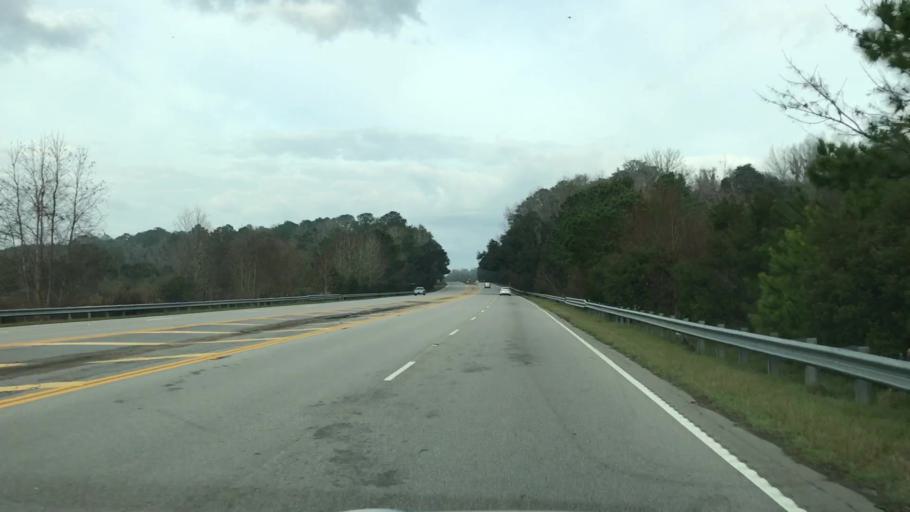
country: US
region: South Carolina
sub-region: Hampton County
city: Yemassee
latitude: 32.6250
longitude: -80.8267
